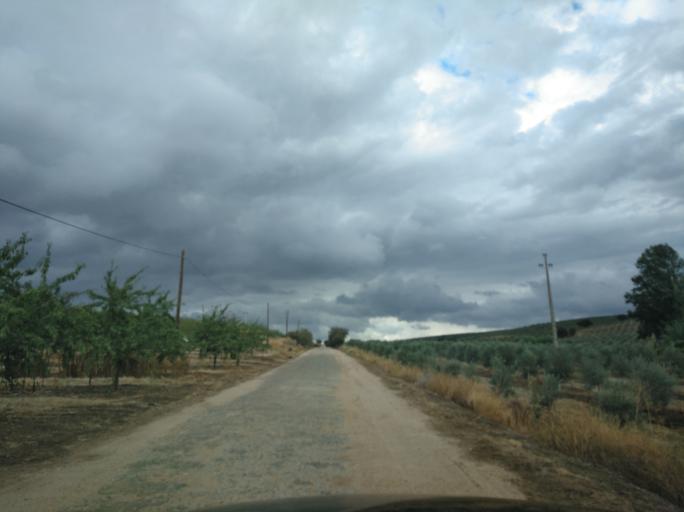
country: PT
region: Portalegre
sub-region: Campo Maior
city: Campo Maior
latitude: 39.0377
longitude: -7.1254
